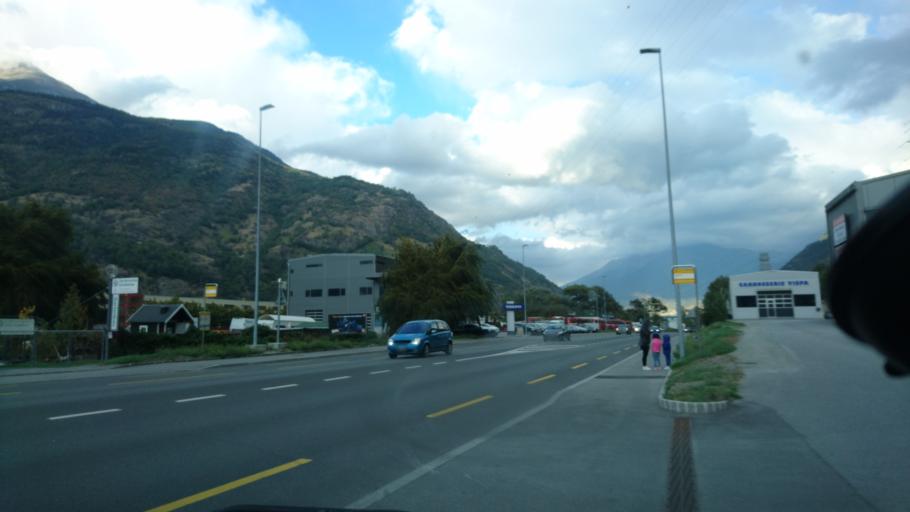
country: CH
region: Valais
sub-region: Visp District
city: Visp
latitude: 46.2931
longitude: 7.8949
